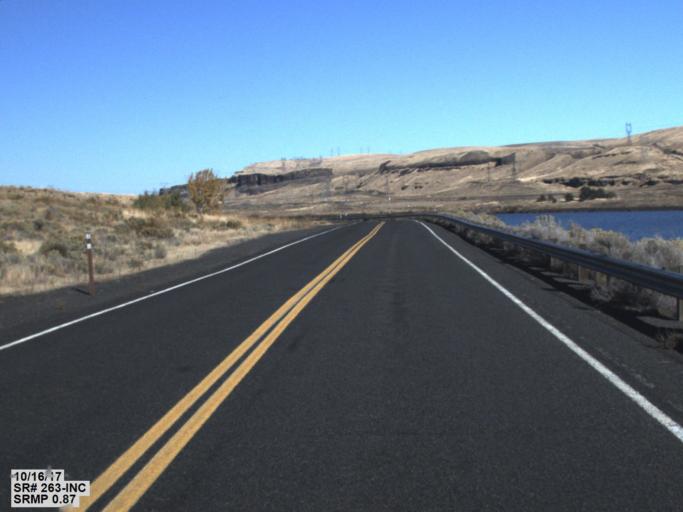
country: US
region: Washington
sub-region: Franklin County
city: Connell
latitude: 46.5362
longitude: -118.5676
